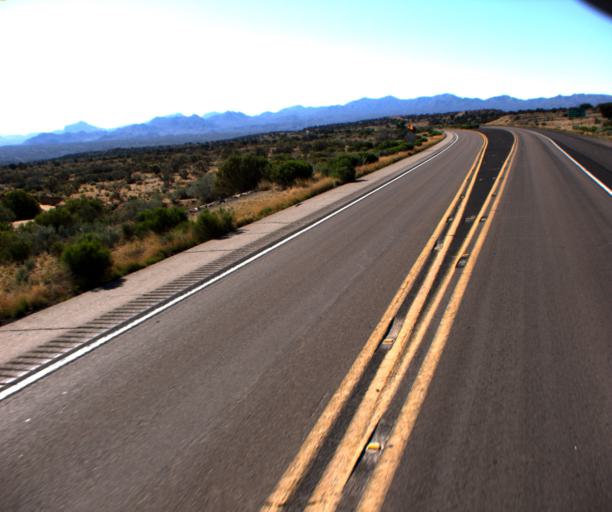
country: US
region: Arizona
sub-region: Mohave County
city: New Kingman-Butler
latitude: 35.1511
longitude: -113.6912
